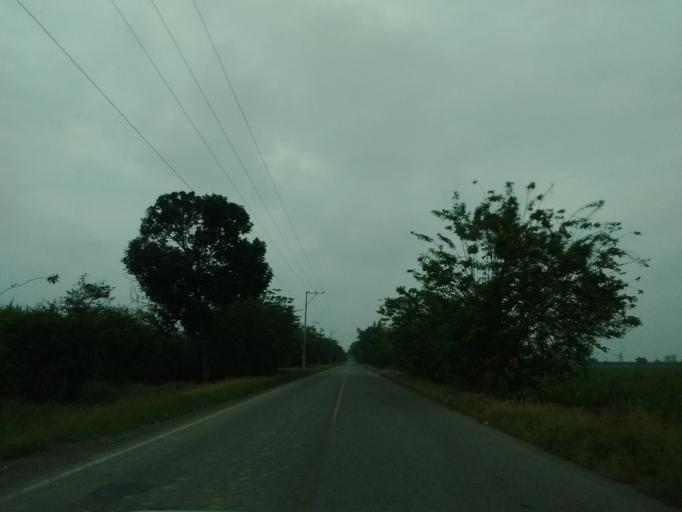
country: CO
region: Cauca
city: Padilla
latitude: 3.2271
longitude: -76.3441
